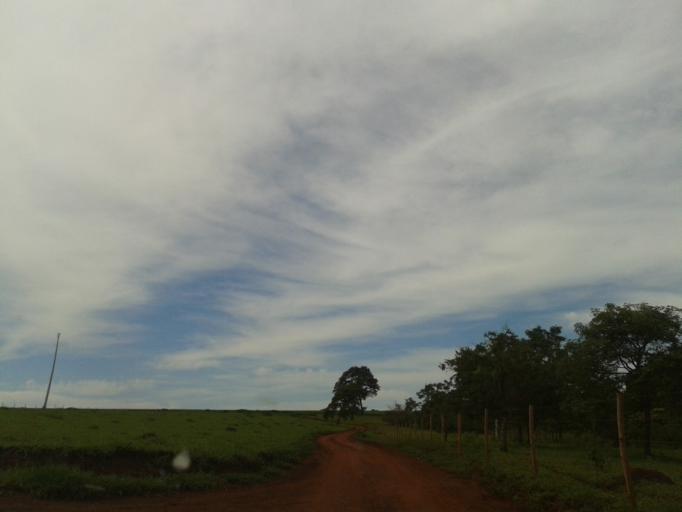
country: BR
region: Minas Gerais
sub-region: Capinopolis
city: Capinopolis
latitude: -18.7566
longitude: -49.8077
